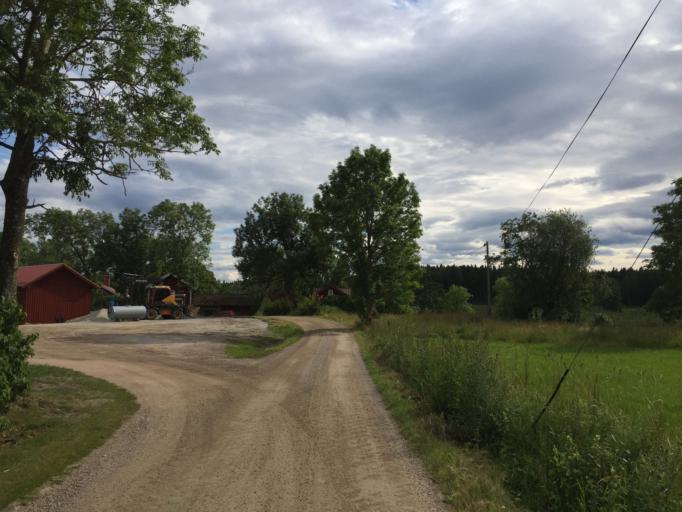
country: SE
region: Vaestmanland
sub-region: Norbergs Kommun
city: Norberg
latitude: 60.0316
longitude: 15.9608
